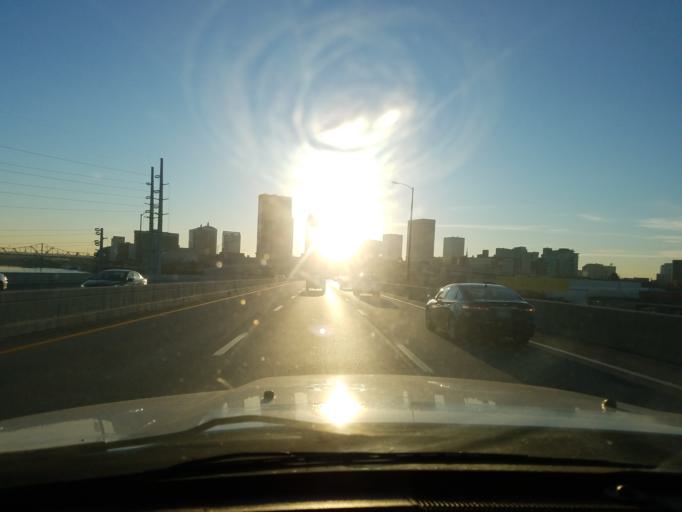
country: US
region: Kentucky
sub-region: Jefferson County
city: Louisville
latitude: 38.2605
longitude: -85.7691
